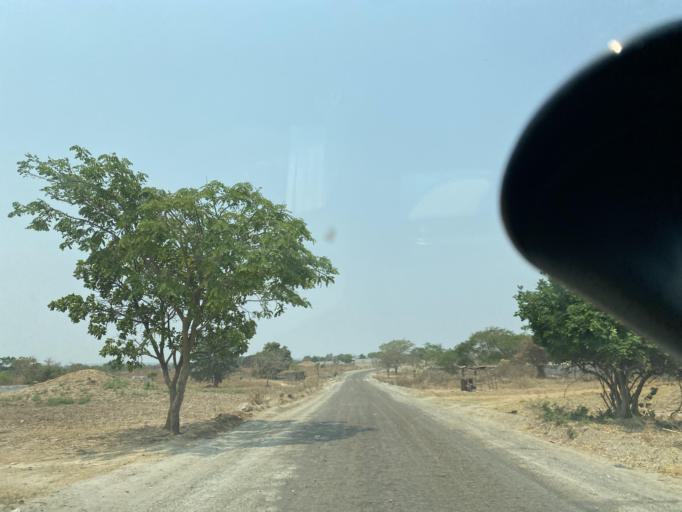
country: ZM
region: Lusaka
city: Lusaka
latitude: -15.5611
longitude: 28.4224
